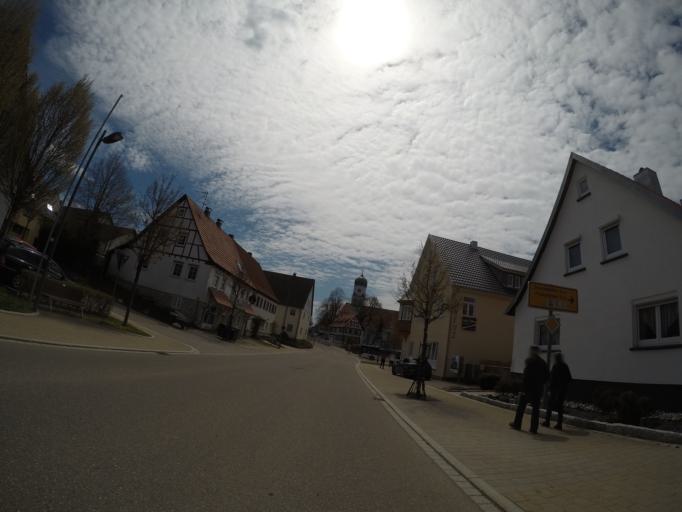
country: DE
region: Baden-Wuerttemberg
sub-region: Tuebingen Region
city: Westerheim
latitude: 48.5156
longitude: 9.6244
